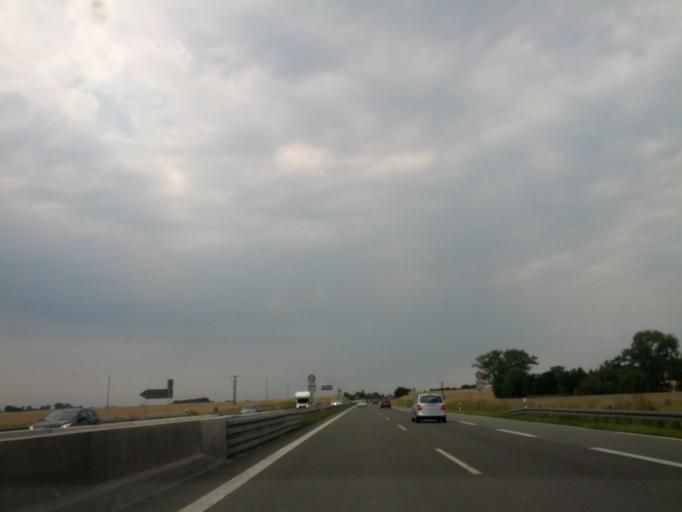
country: DE
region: Brandenburg
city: Fehrbellin
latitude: 52.8497
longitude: 12.7774
